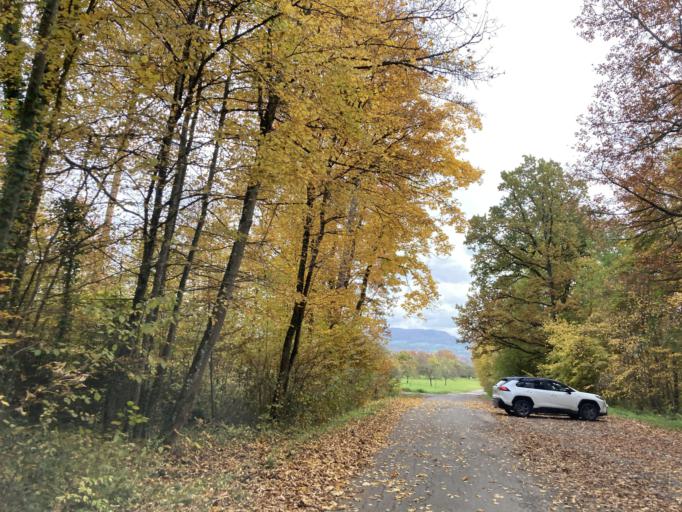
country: DE
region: Baden-Wuerttemberg
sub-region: Tuebingen Region
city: Ofterdingen
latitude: 48.4299
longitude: 9.0092
